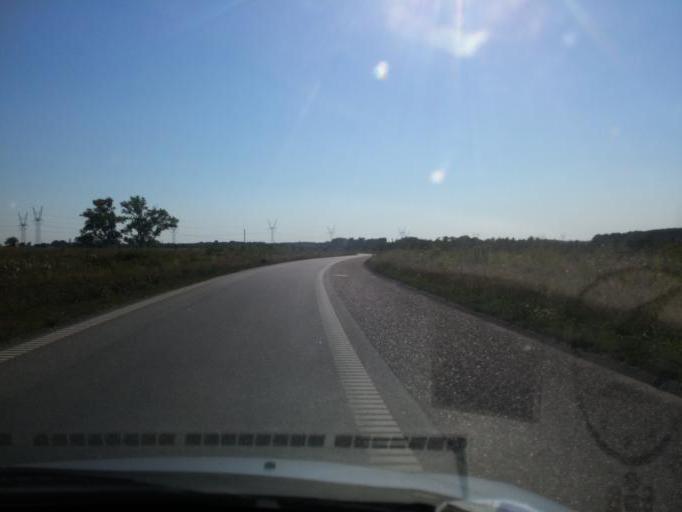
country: DK
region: South Denmark
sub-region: Odense Kommune
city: Neder Holluf
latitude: 55.3529
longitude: 10.4578
